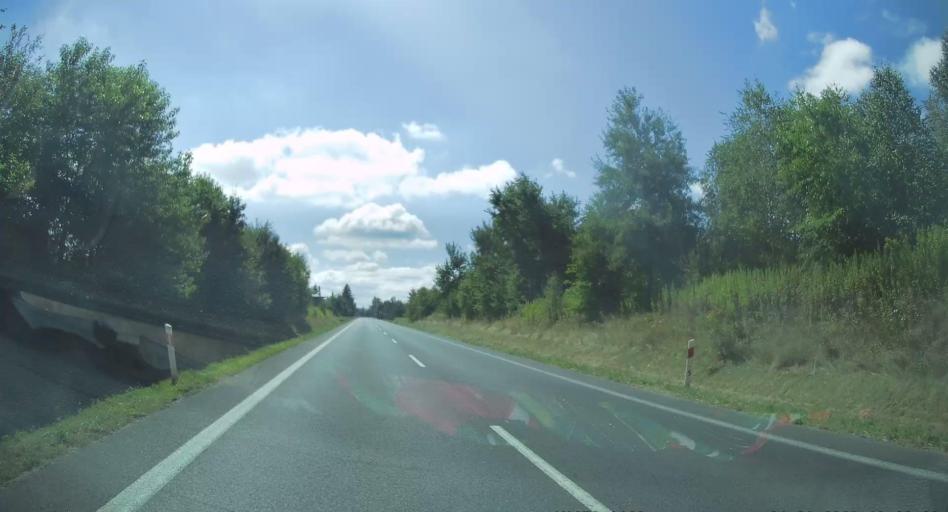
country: PL
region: Subcarpathian Voivodeship
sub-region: Powiat debicki
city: Brzeznica
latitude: 50.1370
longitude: 21.4849
